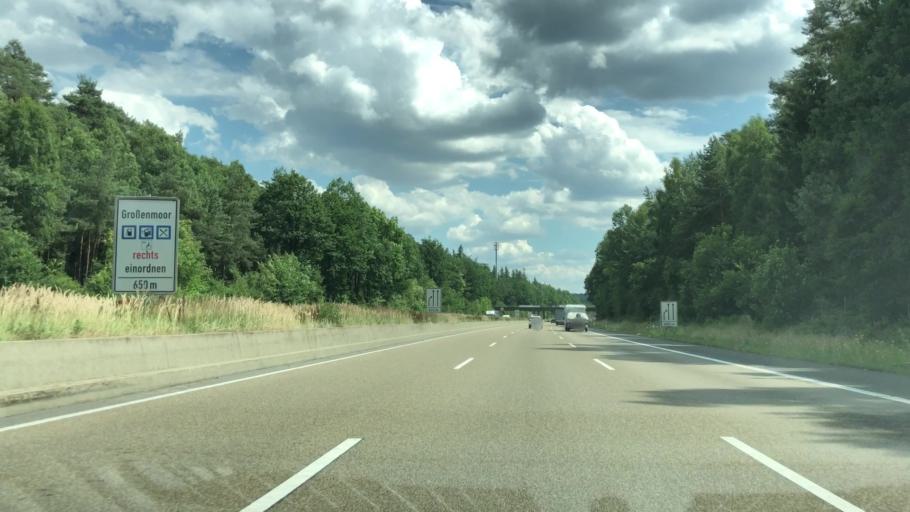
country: DE
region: Hesse
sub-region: Regierungsbezirk Kassel
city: Niederaula
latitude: 50.7420
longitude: 9.6381
